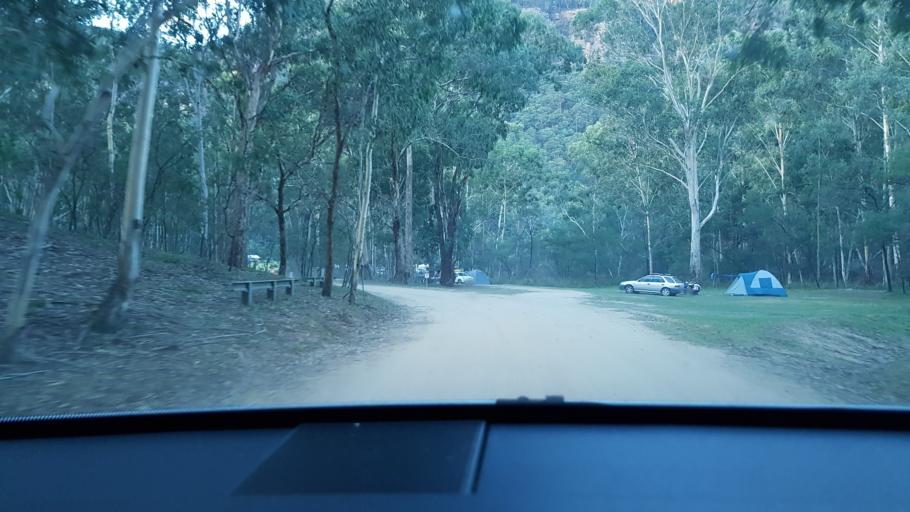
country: AU
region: New South Wales
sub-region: Lithgow
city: Portland
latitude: -33.1740
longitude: 150.2376
